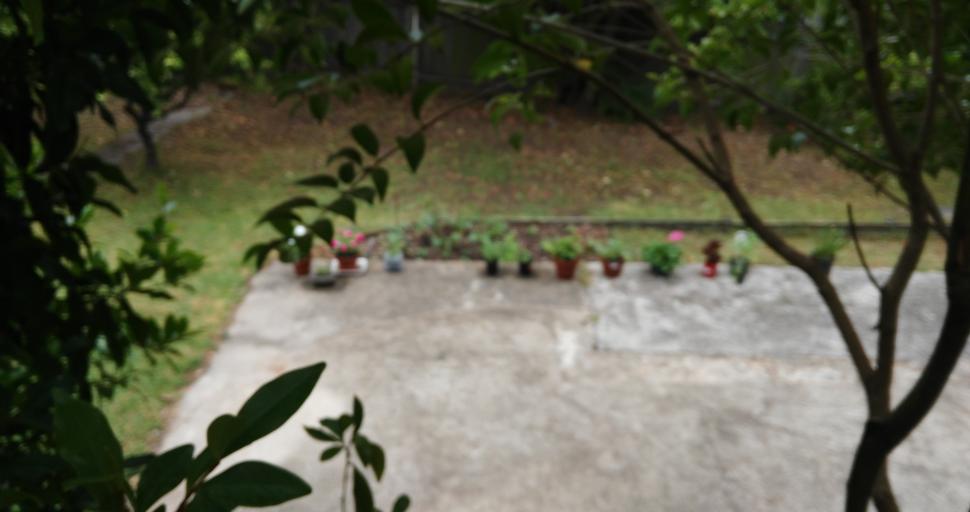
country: AU
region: New South Wales
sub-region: Parramatta
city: Carlingford
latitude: -33.7777
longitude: 151.0499
